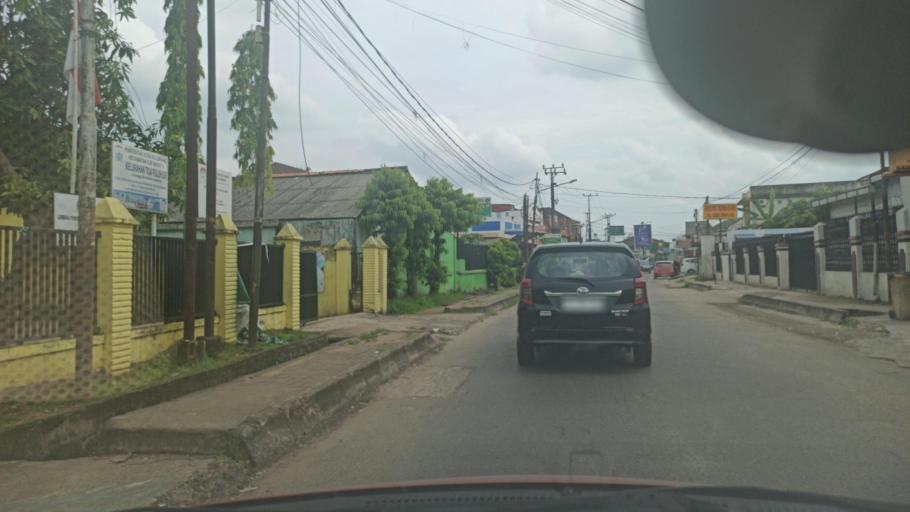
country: ID
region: South Sumatra
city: Plaju
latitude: -2.9972
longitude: 104.7498
